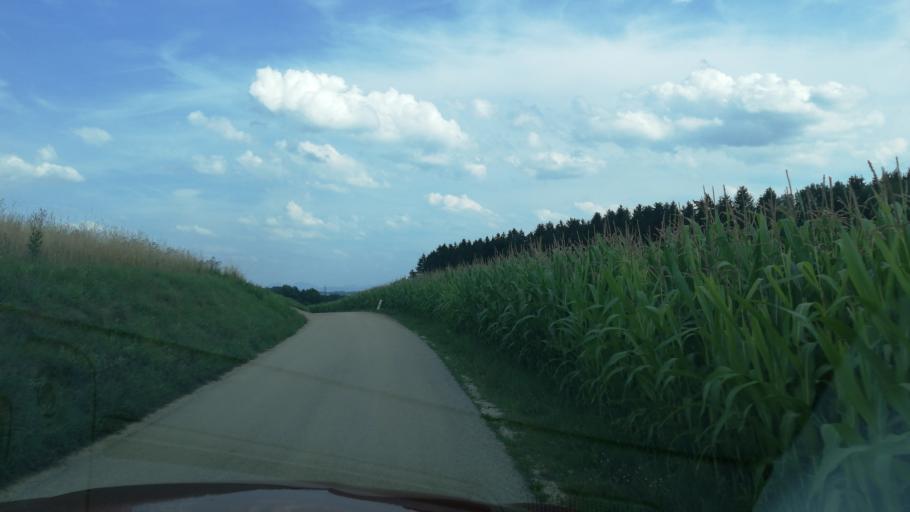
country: AT
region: Upper Austria
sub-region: Wels-Land
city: Pennewang
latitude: 48.1055
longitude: 13.8482
